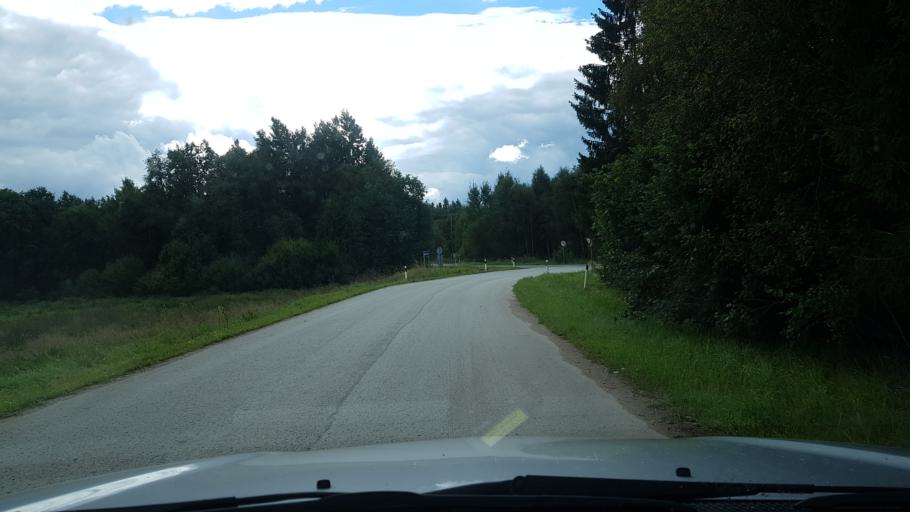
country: EE
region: Harju
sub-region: Rae vald
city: Vaida
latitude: 59.2628
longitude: 25.0495
